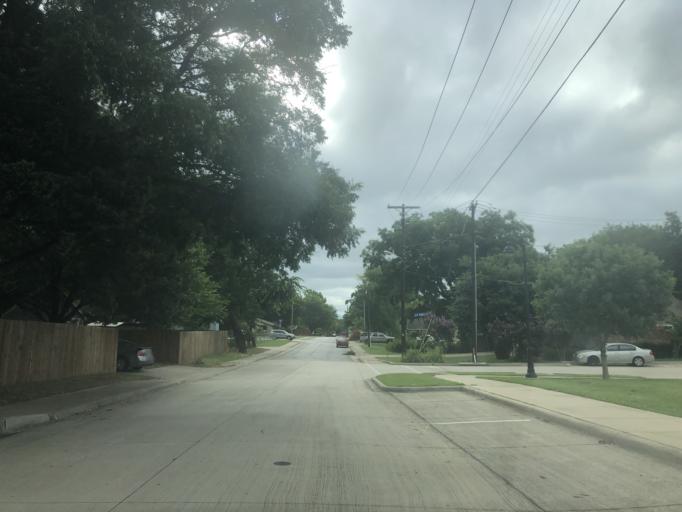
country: US
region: Texas
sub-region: Dallas County
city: Duncanville
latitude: 32.6526
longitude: -96.9066
